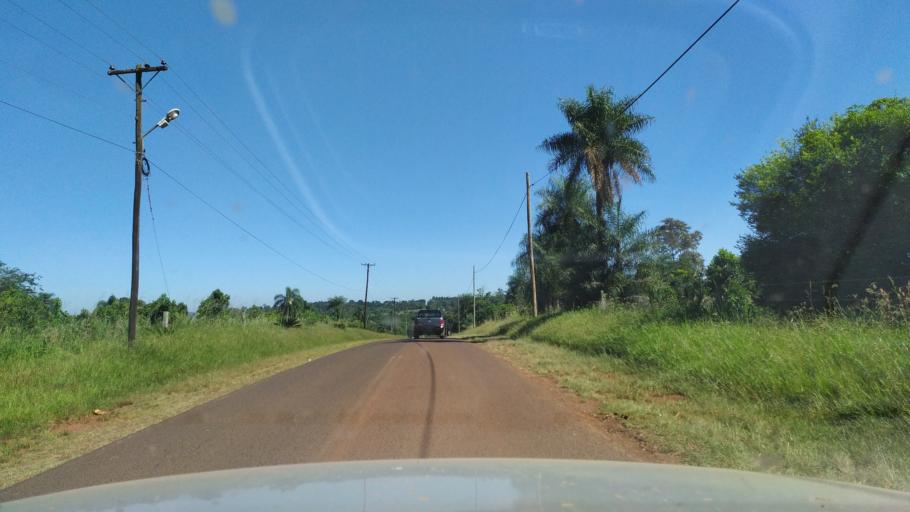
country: AR
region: Misiones
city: Caraguatay
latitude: -26.6468
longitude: -54.7485
